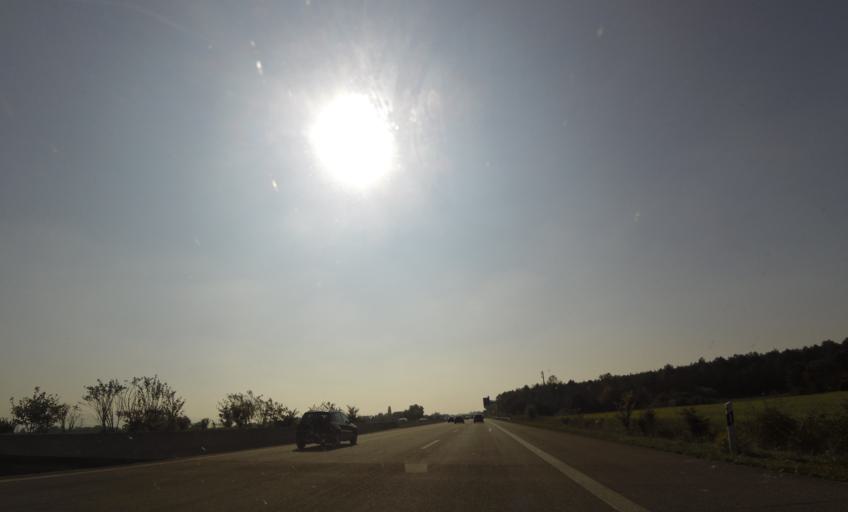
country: DE
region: Baden-Wuerttemberg
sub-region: Freiburg Region
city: Appenweier
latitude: 48.5681
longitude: 7.9601
